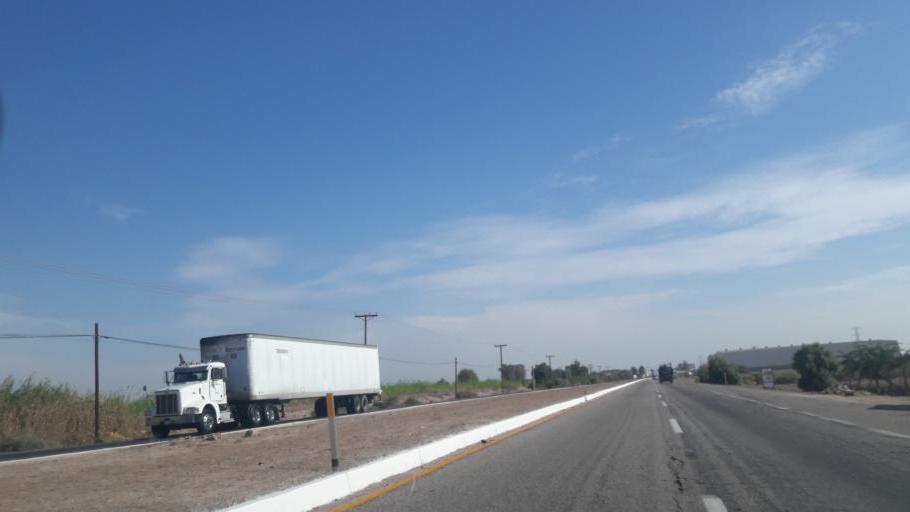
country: MX
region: Baja California
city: Progreso
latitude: 32.5852
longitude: -115.5962
